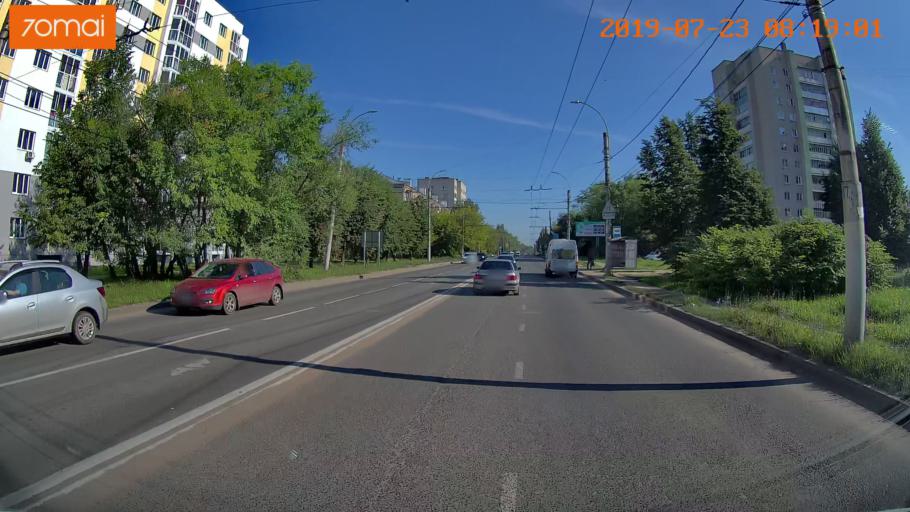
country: RU
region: Ivanovo
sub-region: Gorod Ivanovo
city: Ivanovo
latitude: 56.9656
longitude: 40.9624
